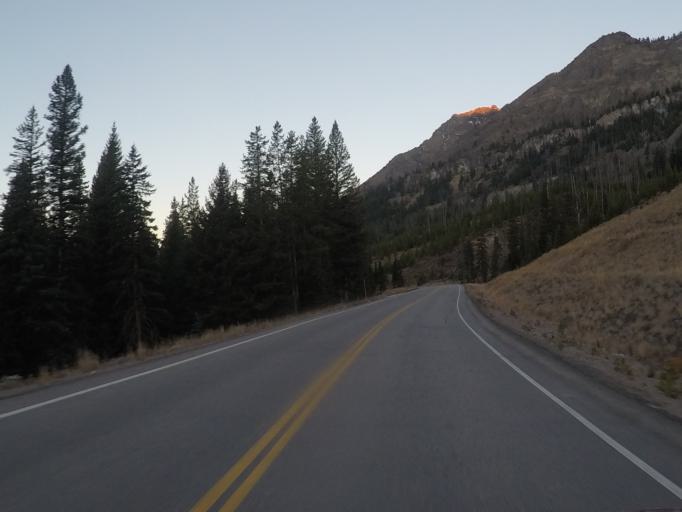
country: US
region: Montana
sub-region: Stillwater County
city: Absarokee
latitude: 45.0183
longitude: -109.9584
